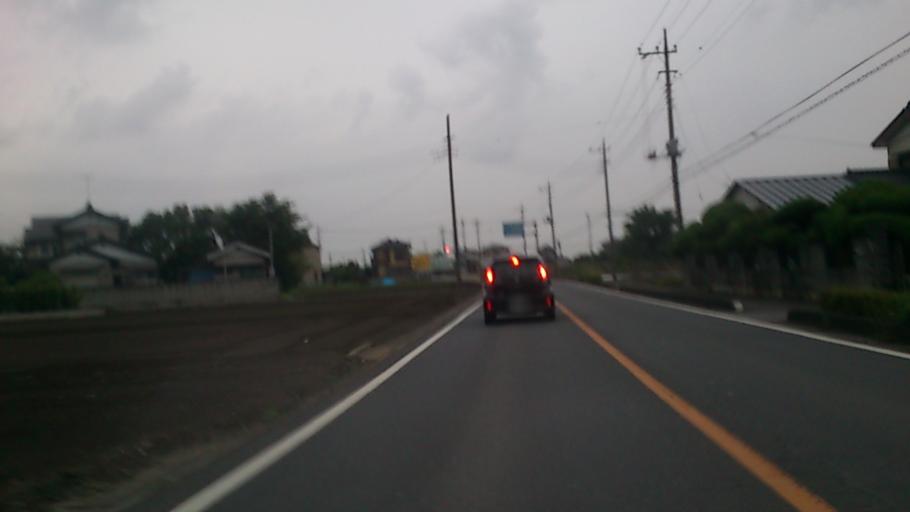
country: JP
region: Saitama
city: Kazo
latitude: 36.1622
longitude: 139.5999
